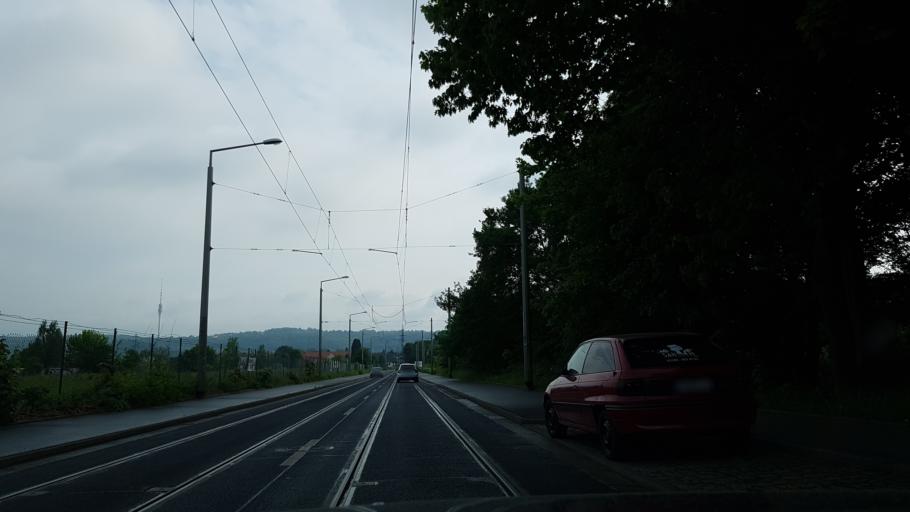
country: DE
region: Saxony
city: Heidenau
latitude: 51.0142
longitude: 13.8251
